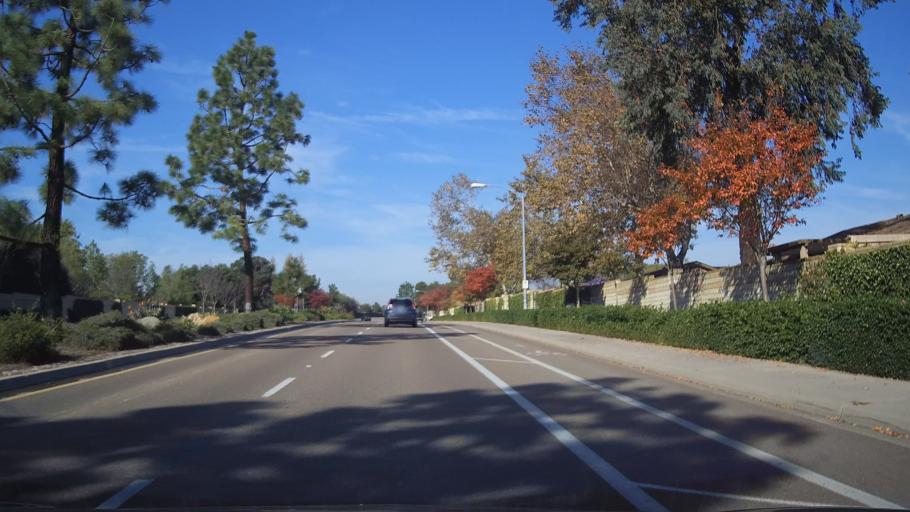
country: US
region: California
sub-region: San Diego County
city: La Mesa
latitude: 32.8109
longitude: -117.1055
